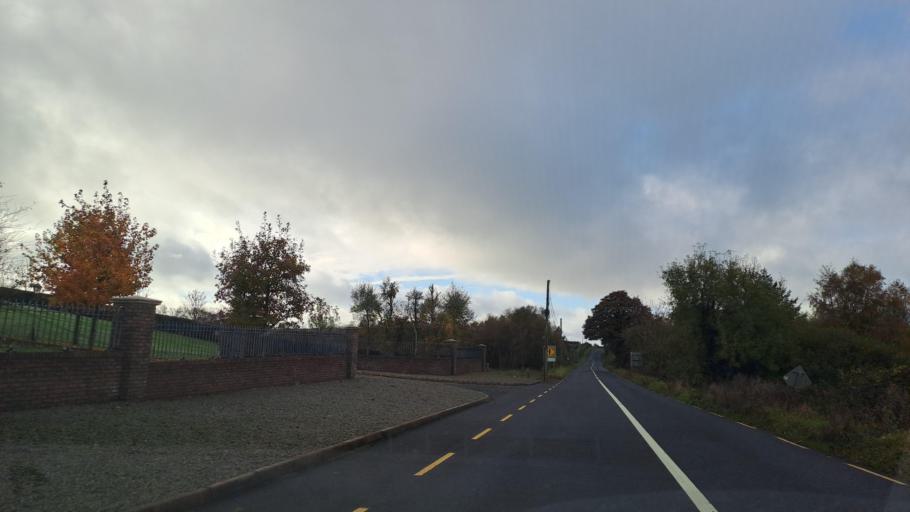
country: IE
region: Ulster
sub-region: An Cabhan
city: Virginia
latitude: 53.8542
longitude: -7.0493
